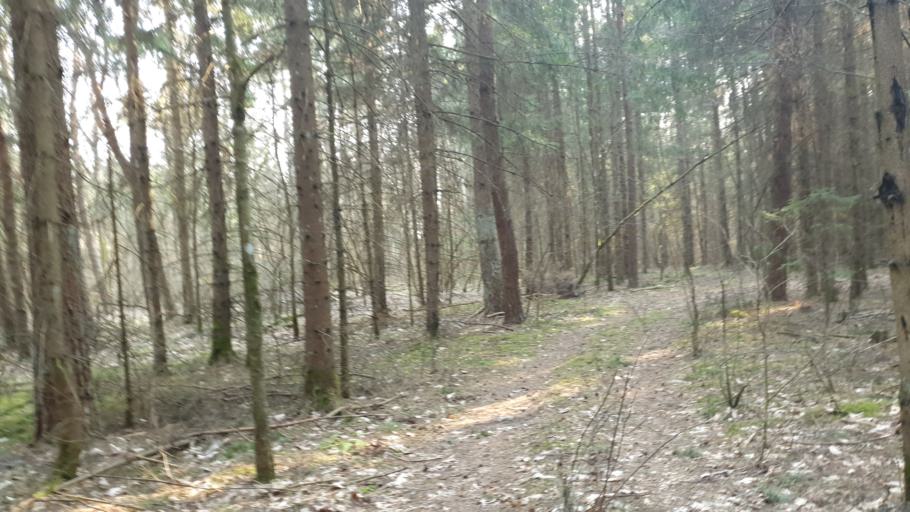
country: LT
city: Nemencine
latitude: 54.8744
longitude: 25.5719
